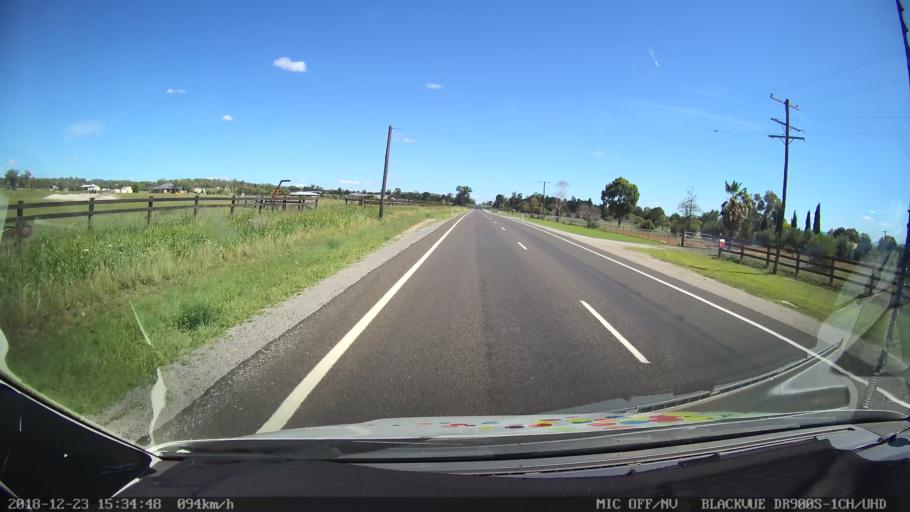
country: AU
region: New South Wales
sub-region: Tamworth Municipality
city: Tamworth
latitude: -31.0188
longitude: 150.8799
